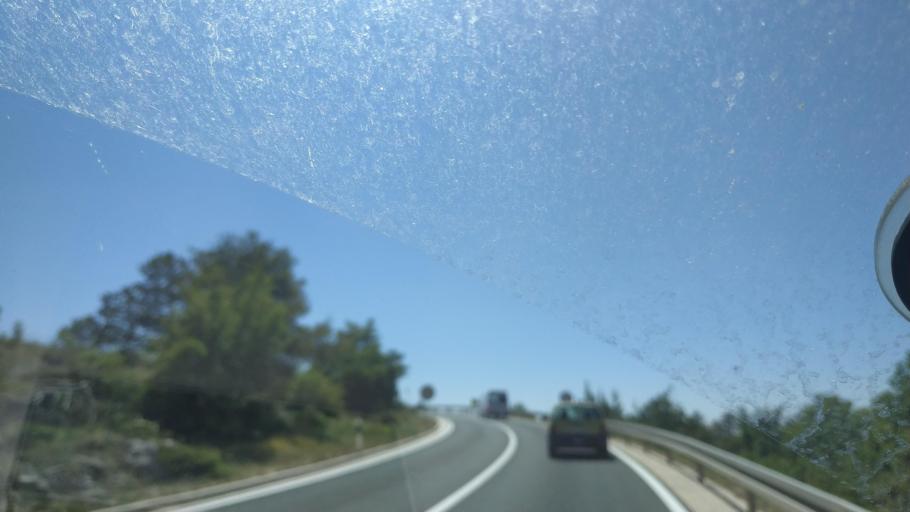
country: HR
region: Sibensko-Kniniska
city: Drnis
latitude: 43.8513
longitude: 16.1531
